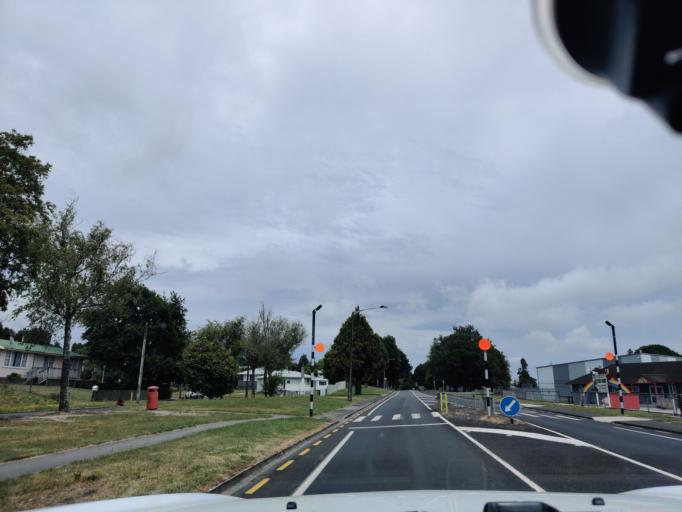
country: NZ
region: Waikato
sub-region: South Waikato District
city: Tokoroa
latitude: -38.2289
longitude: 175.8637
